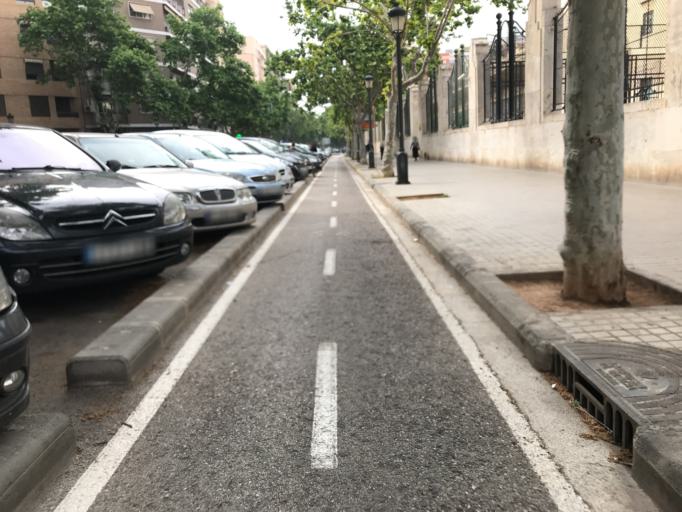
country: ES
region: Valencia
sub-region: Provincia de Valencia
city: Valencia
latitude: 39.4688
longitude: -0.3880
